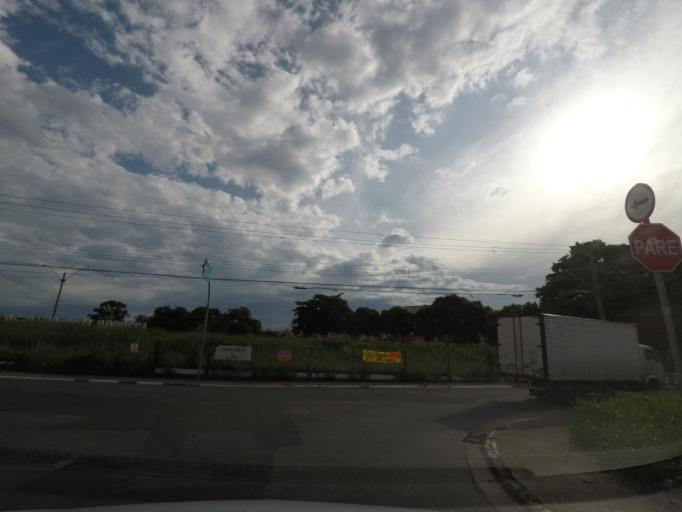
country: BR
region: Sao Paulo
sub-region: Campinas
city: Campinas
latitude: -22.9077
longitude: -47.1142
